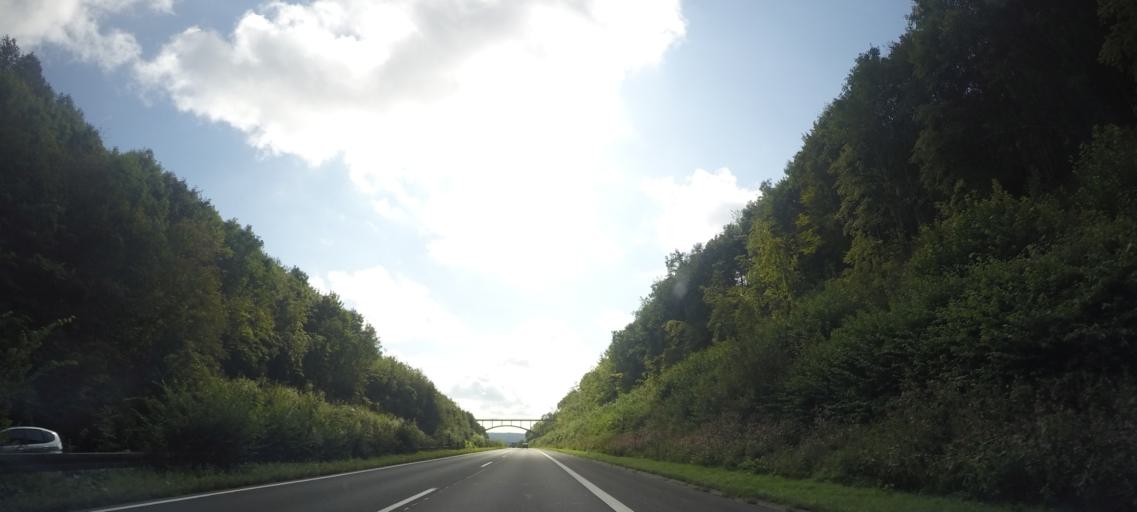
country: DE
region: North Rhine-Westphalia
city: Wickede
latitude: 51.5130
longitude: 7.9050
